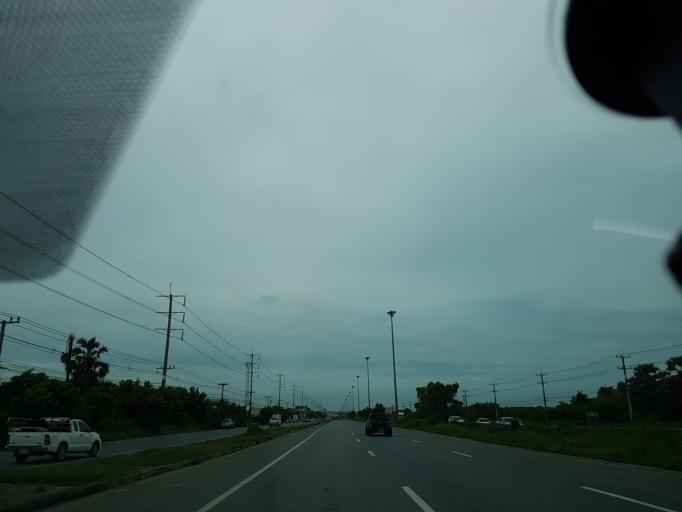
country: TH
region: Pathum Thani
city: Sam Khok
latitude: 14.0474
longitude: 100.5664
